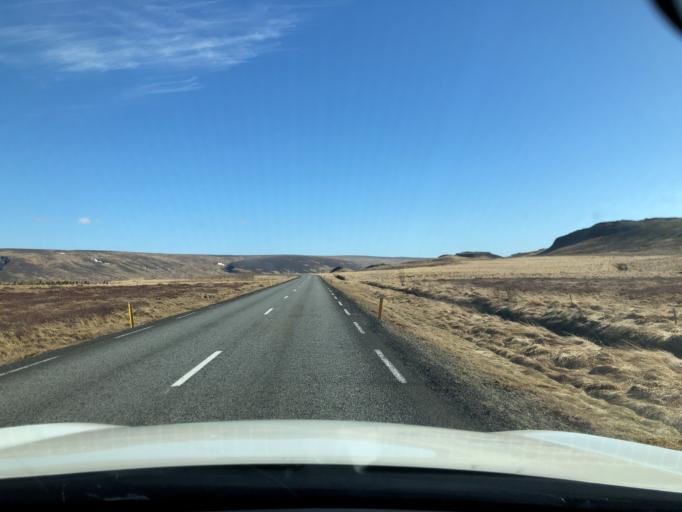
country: IS
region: South
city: Hveragerdi
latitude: 64.6791
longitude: -21.2484
